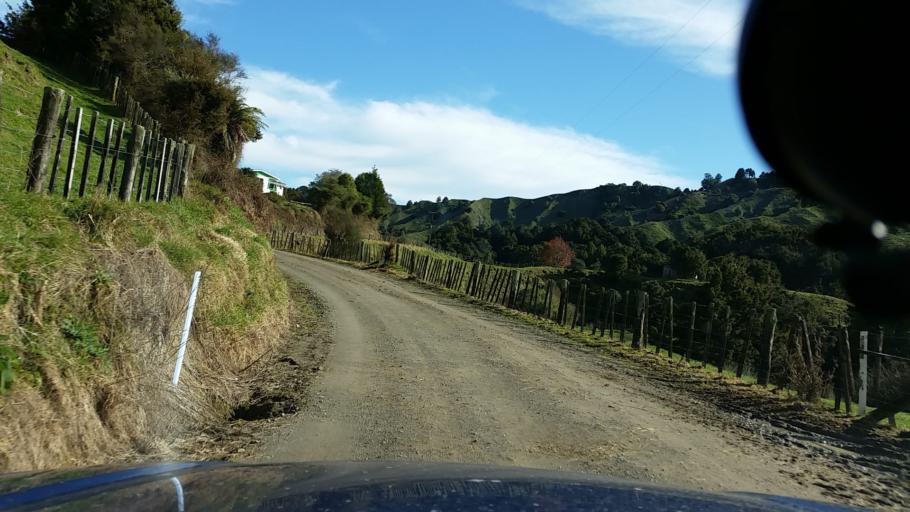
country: NZ
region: Taranaki
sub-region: New Plymouth District
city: Waitara
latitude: -39.0504
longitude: 174.7666
